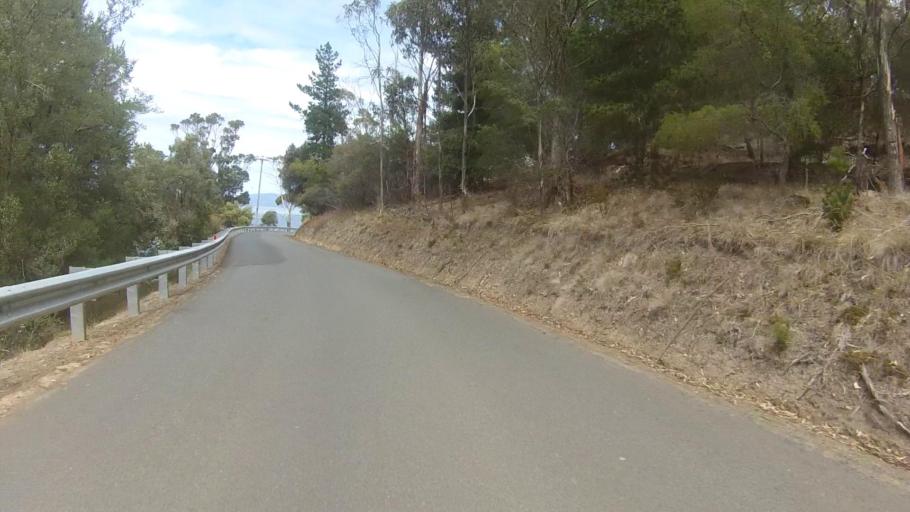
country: AU
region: Tasmania
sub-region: Kingborough
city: Blackmans Bay
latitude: -43.0553
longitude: 147.3352
